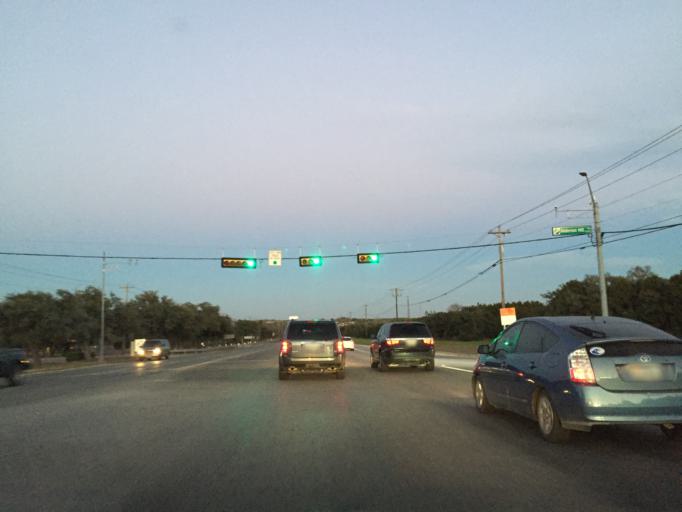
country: US
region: Texas
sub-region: Williamson County
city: Cedar Park
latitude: 30.5122
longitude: -97.8582
